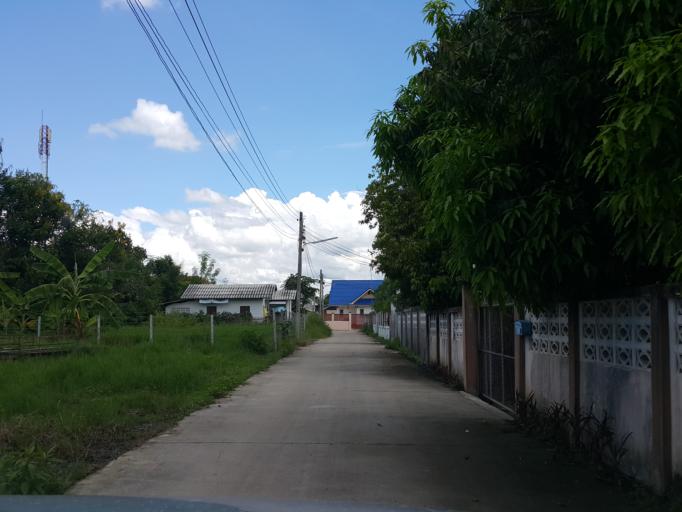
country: TH
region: Chiang Mai
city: San Kamphaeng
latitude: 18.7590
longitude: 99.1274
